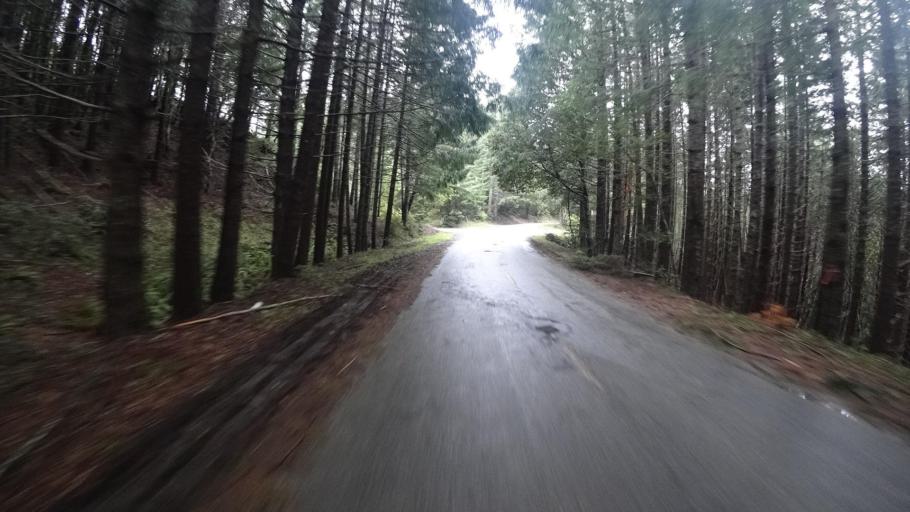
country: US
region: California
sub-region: Humboldt County
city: Westhaven-Moonstone
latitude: 41.2236
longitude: -123.9606
